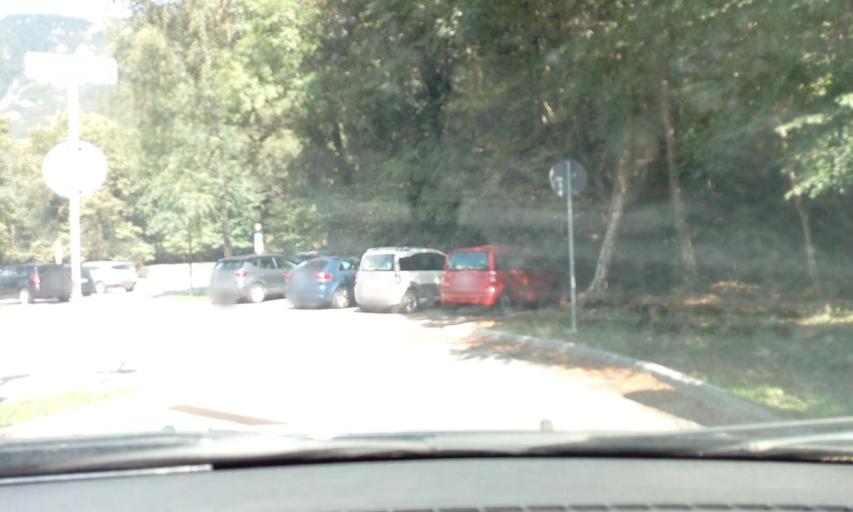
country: IT
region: Friuli Venezia Giulia
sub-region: Provincia di Udine
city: Bordano
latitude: 46.3188
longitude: 13.0687
